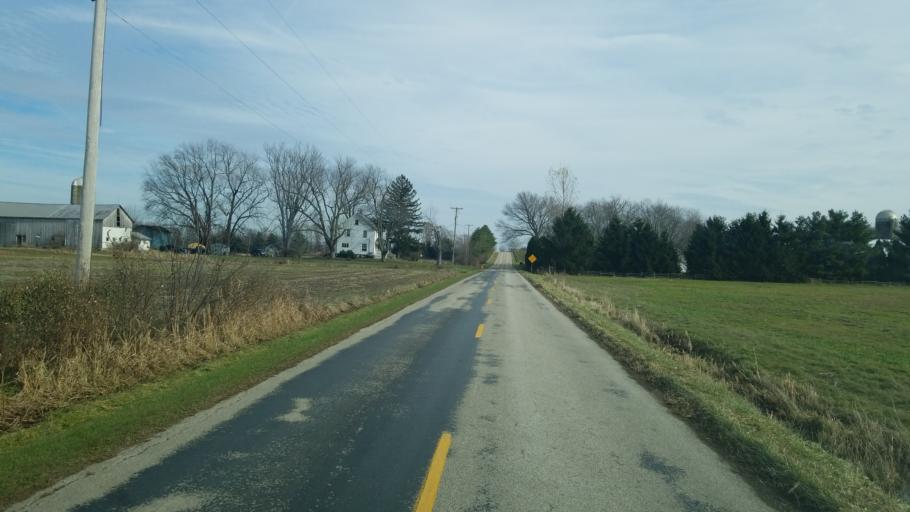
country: US
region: Ohio
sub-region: Ashtabula County
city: Roaming Shores
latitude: 41.6351
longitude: -80.7193
